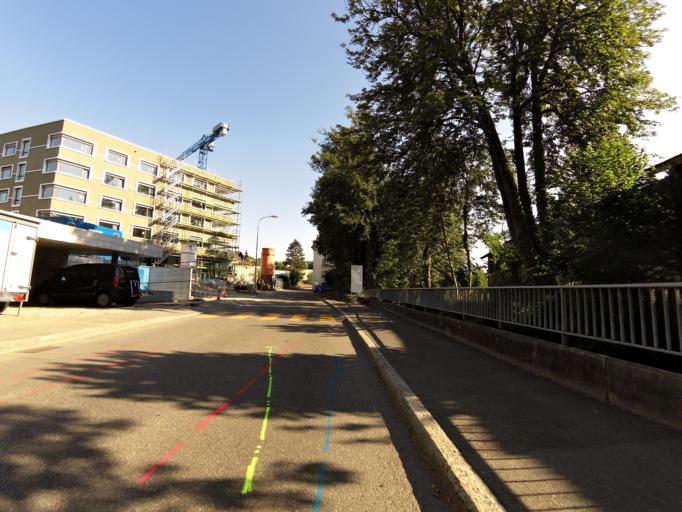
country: CH
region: Aargau
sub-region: Bezirk Lenzburg
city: Lenzburg
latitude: 47.3855
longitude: 8.1763
